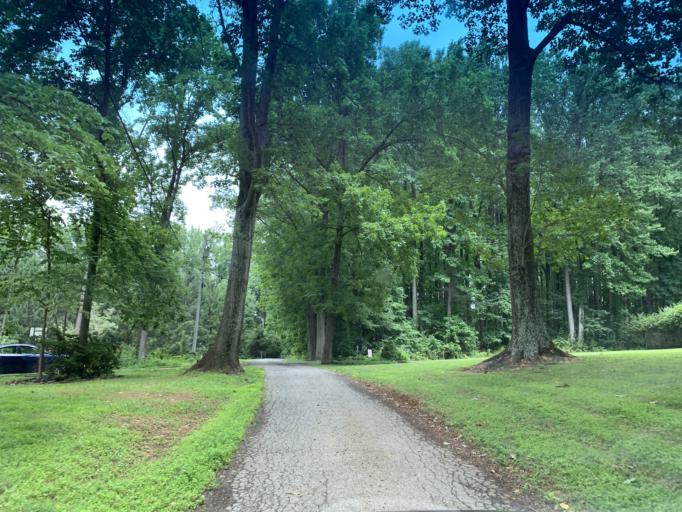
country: US
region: Maryland
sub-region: Baltimore County
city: Kingsville
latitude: 39.4465
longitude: -76.4505
